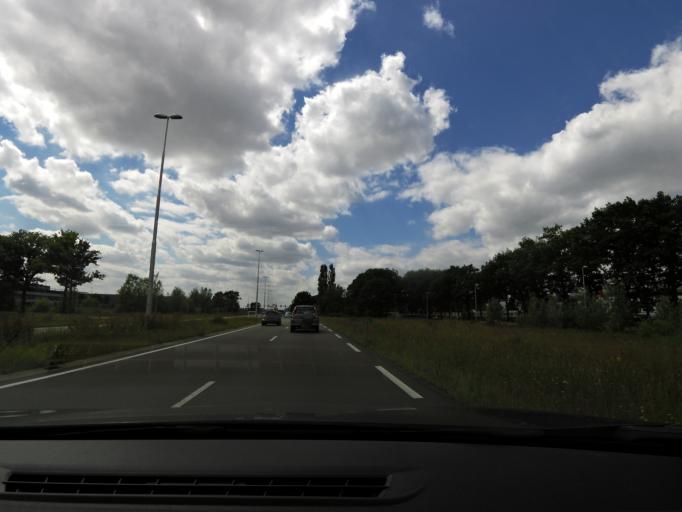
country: NL
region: North Brabant
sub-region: Gemeente Dongen
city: Dongen
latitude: 51.6075
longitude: 5.0006
